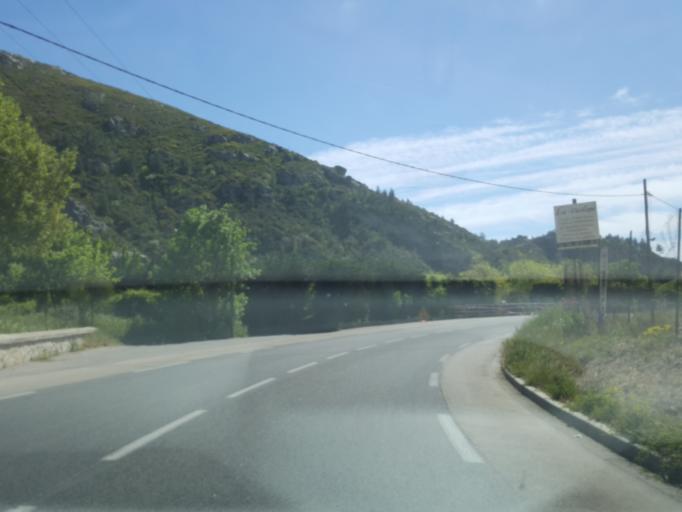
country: FR
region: Provence-Alpes-Cote d'Azur
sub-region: Departement des Bouches-du-Rhone
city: Roquevaire
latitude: 43.3562
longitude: 5.6096
